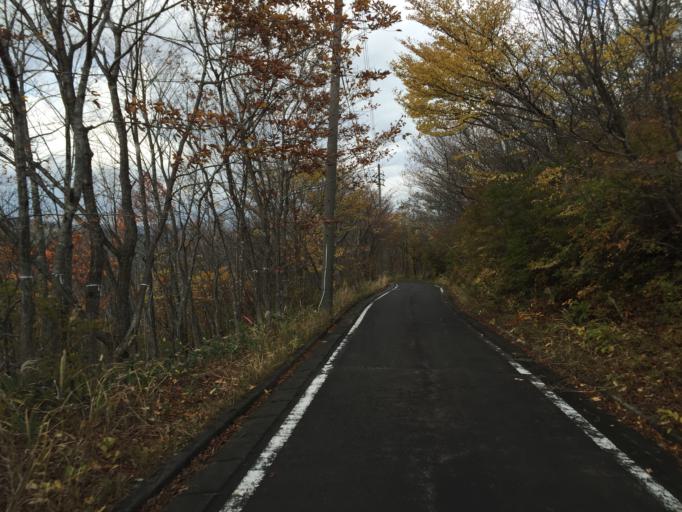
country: JP
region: Fukushima
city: Fukushima-shi
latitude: 37.7315
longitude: 140.3081
